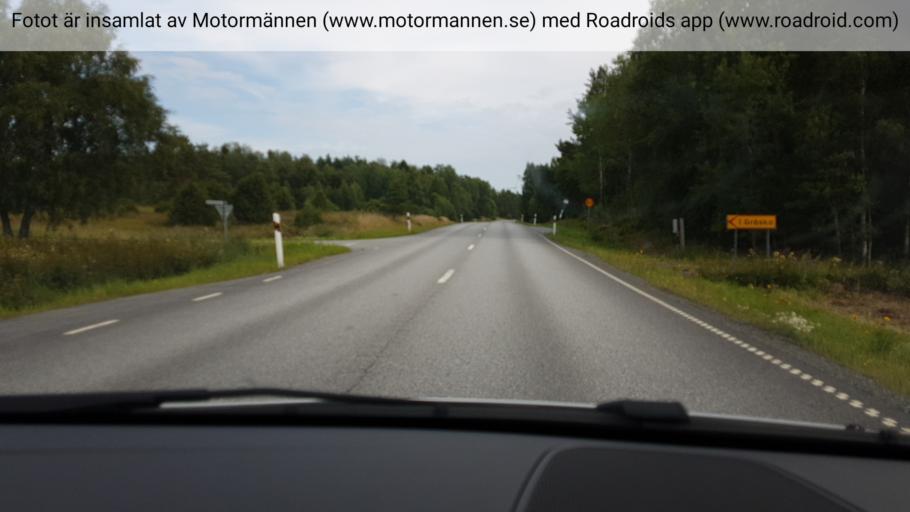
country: SE
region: Stockholm
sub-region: Norrtalje Kommun
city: Hallstavik
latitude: 60.0801
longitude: 18.5116
